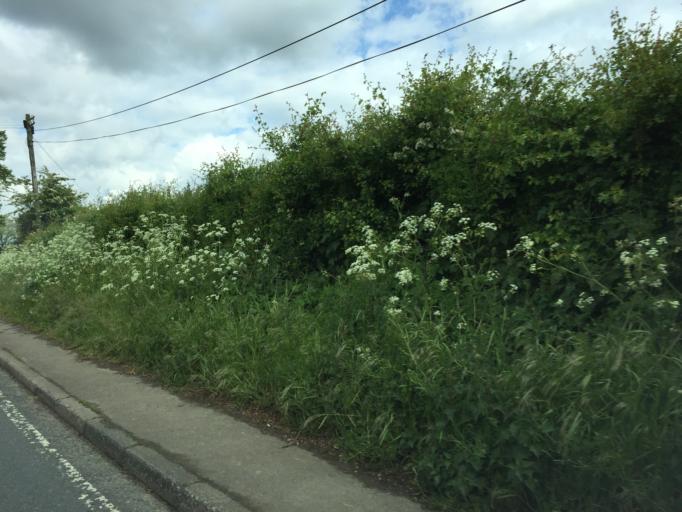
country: GB
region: England
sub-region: Gloucestershire
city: Stonehouse
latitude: 51.7739
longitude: -2.2891
